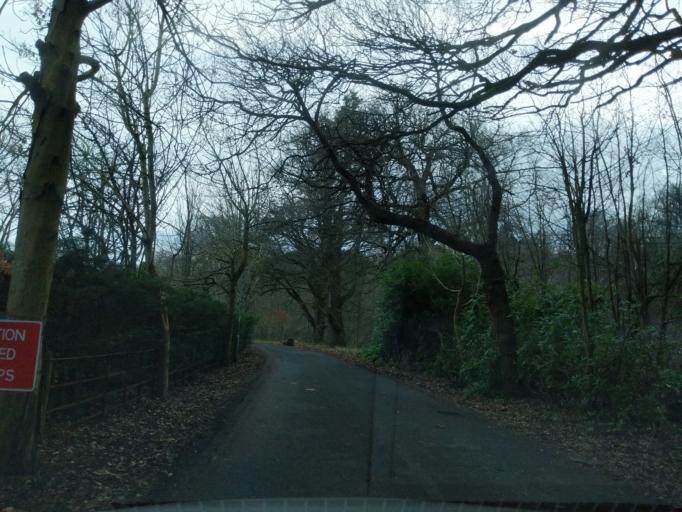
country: GB
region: Scotland
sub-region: South Lanarkshire
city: Carluke
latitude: 55.6966
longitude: -3.8662
